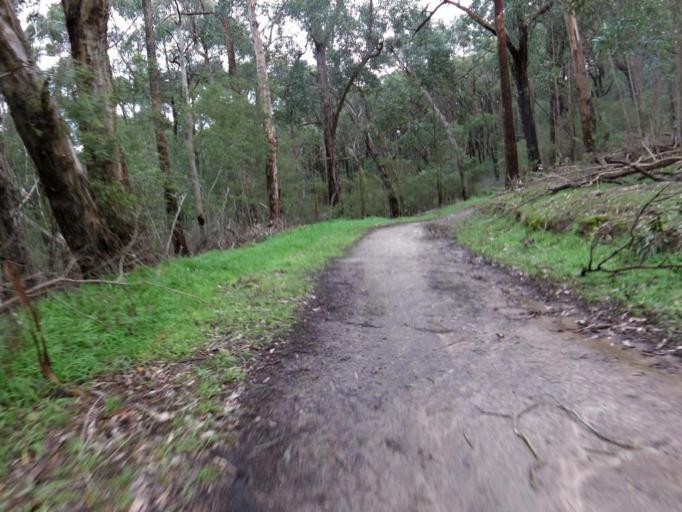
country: AU
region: Victoria
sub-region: Yarra Ranges
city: Lysterfield
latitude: -37.9316
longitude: 145.2835
